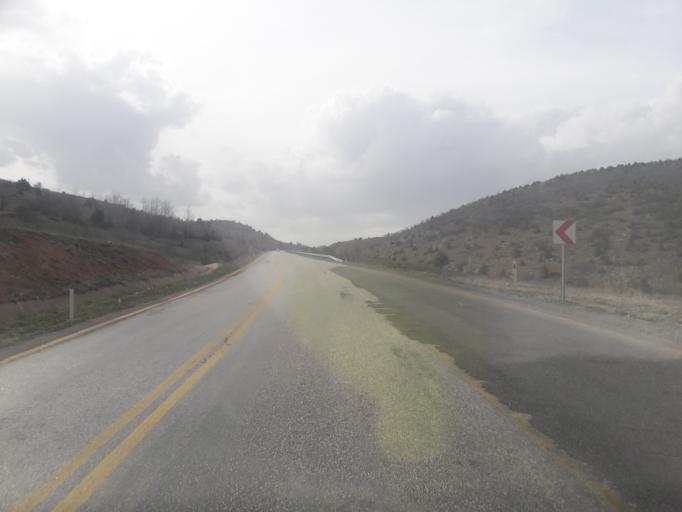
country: TR
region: Gumushane
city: Evren
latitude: 40.1605
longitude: 39.2887
